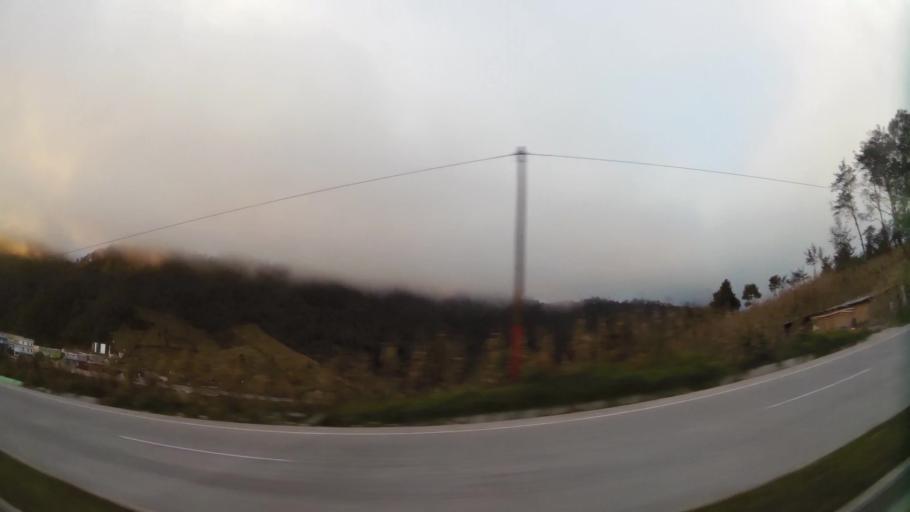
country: GT
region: Solola
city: Concepcion
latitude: 14.8390
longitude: -91.1359
